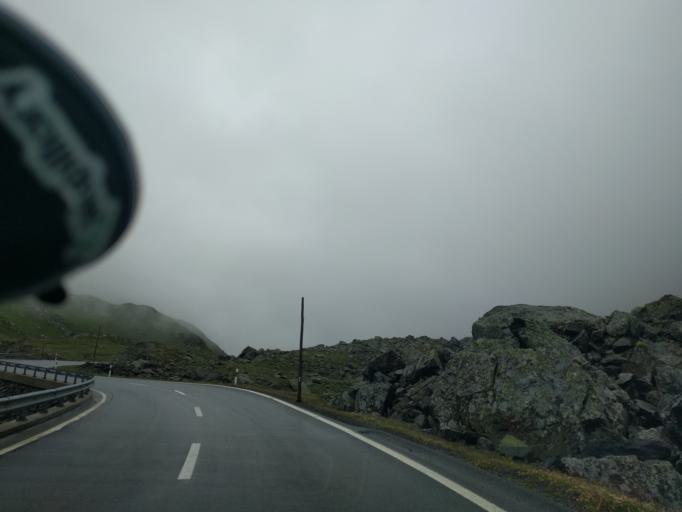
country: CH
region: Grisons
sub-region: Praettigau/Davos District
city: Davos
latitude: 46.7540
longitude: 9.9415
